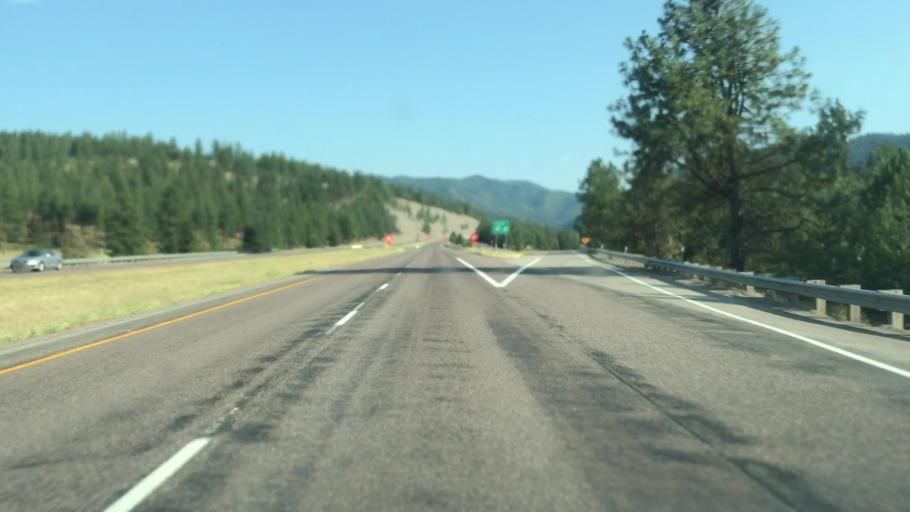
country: US
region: Montana
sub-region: Mineral County
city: Superior
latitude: 47.0286
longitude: -114.7412
